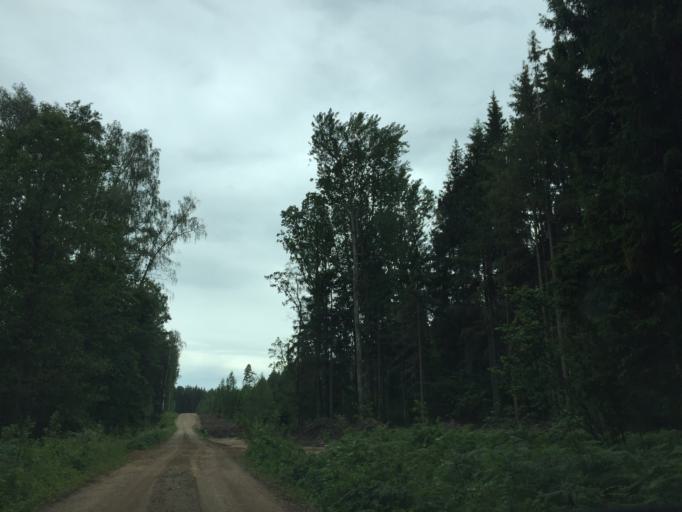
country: LV
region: Tukuma Rajons
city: Tukums
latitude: 57.0079
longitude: 23.1157
